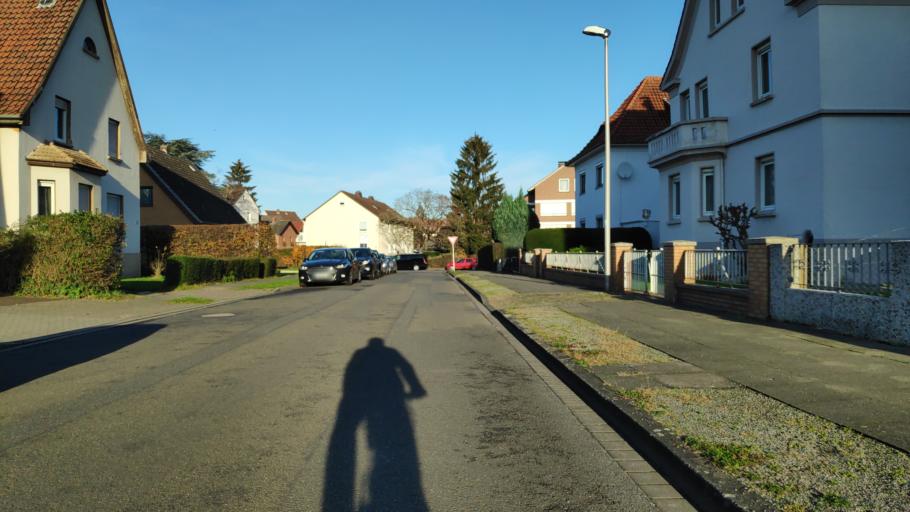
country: DE
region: North Rhine-Westphalia
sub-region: Regierungsbezirk Detmold
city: Minden
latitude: 52.2840
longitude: 8.8967
